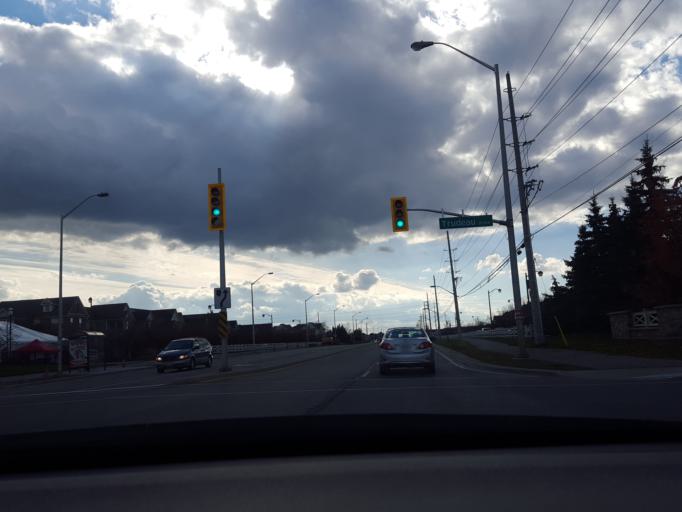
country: CA
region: Ontario
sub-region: Halton
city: Milton
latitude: 43.5282
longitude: -79.8380
